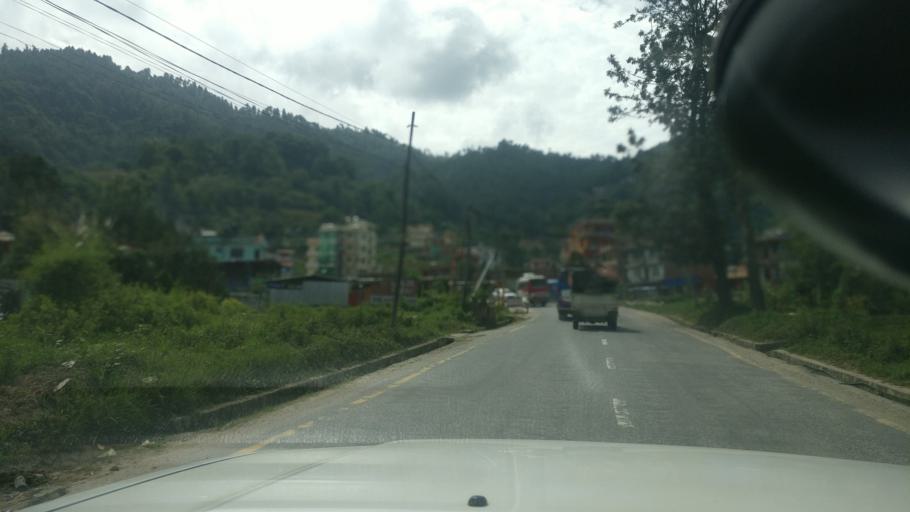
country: NP
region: Central Region
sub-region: Bagmati Zone
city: kankrabari Dovan
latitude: 27.6450
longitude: 85.4655
